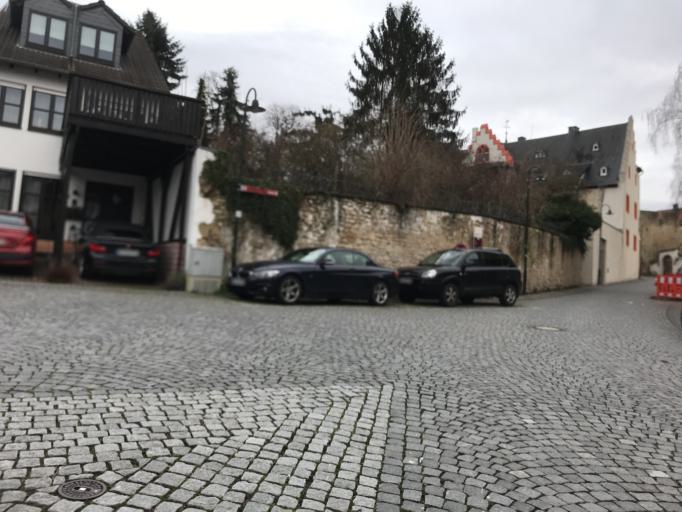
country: DE
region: Rheinland-Pfalz
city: Ingelheim am Rhein
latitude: 49.9640
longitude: 8.0616
